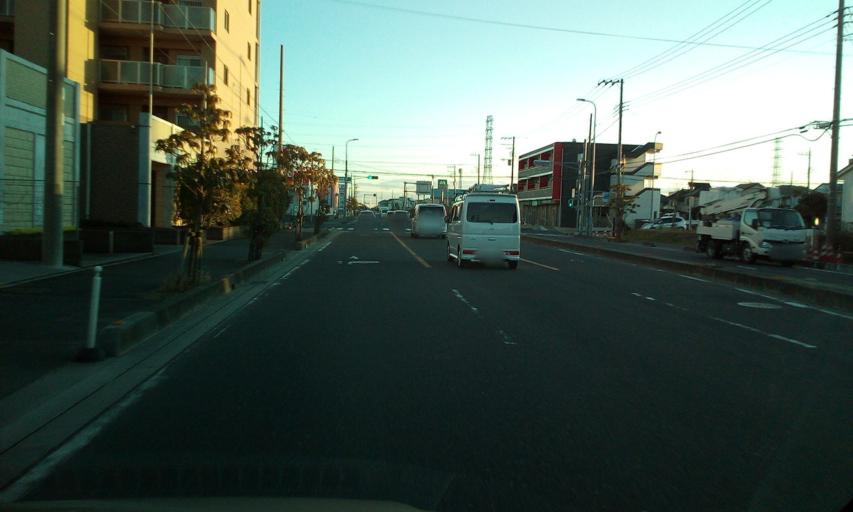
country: JP
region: Saitama
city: Yoshikawa
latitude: 35.8654
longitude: 139.8483
